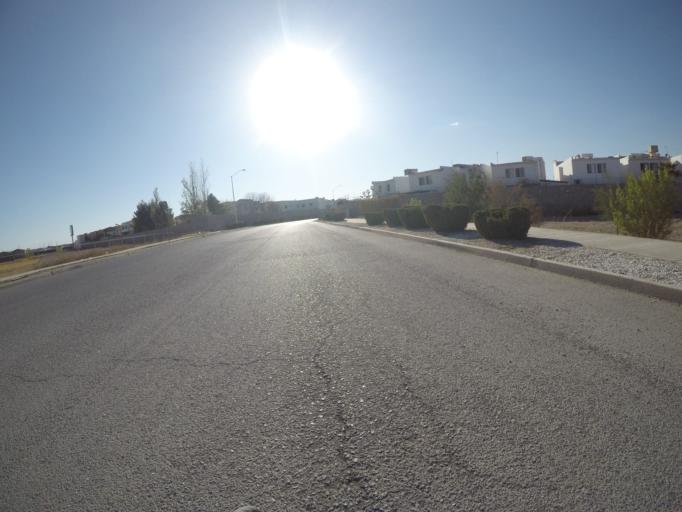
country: MX
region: Chihuahua
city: Ciudad Juarez
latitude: 31.7030
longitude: -106.3954
